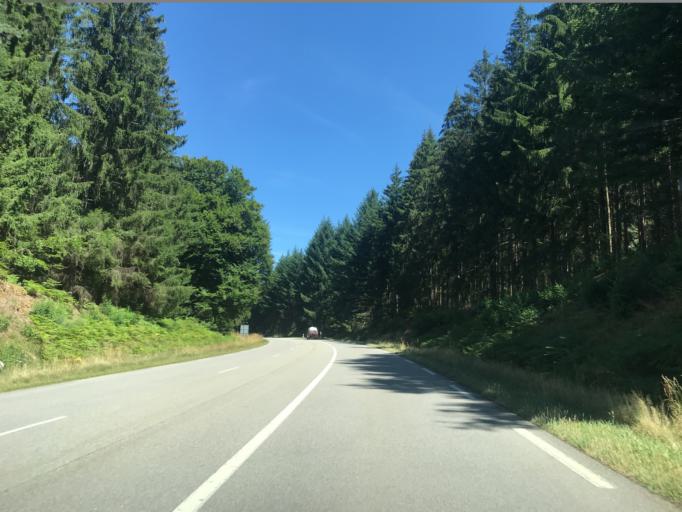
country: FR
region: Limousin
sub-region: Departement de la Correze
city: Meymac
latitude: 45.4784
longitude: 2.1912
